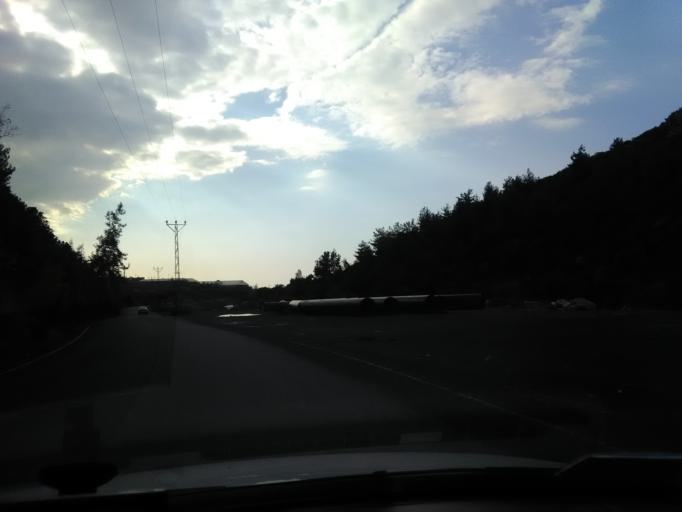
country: TR
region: Antalya
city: Gazipasa
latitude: 36.2798
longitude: 32.3607
